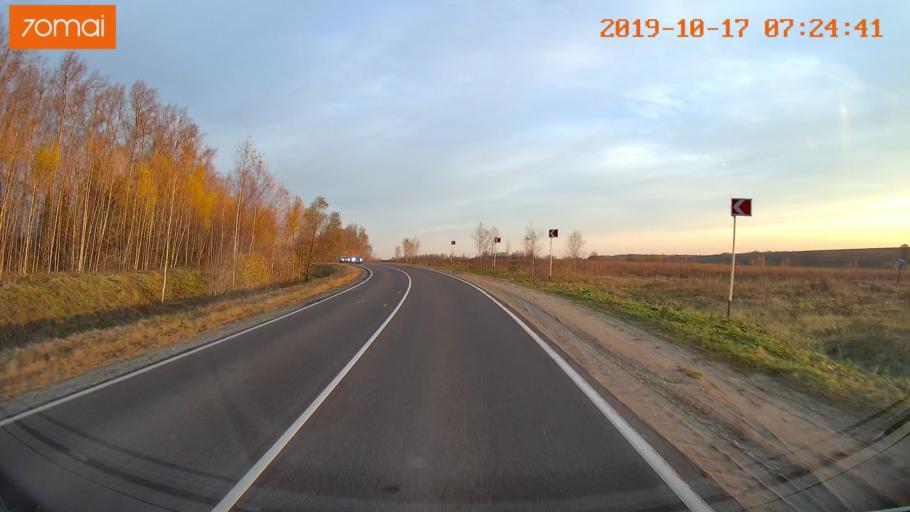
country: RU
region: Ivanovo
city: Gavrilov Posad
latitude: 56.3418
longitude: 40.1127
